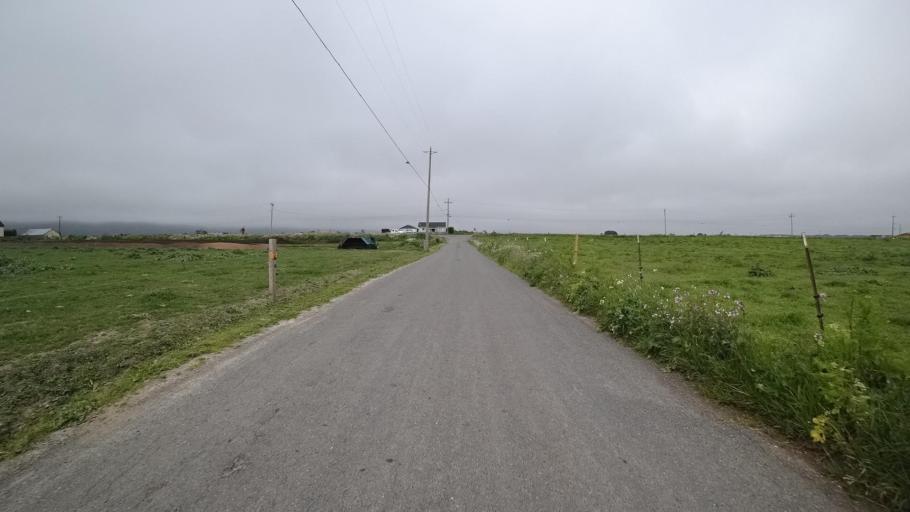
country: US
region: California
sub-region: Humboldt County
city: Fortuna
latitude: 40.5917
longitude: -124.2011
